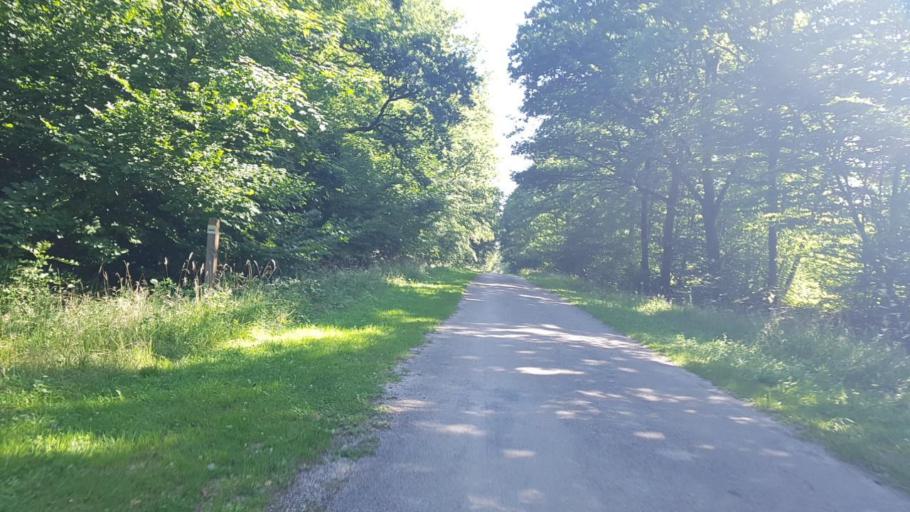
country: FR
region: Picardie
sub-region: Departement de l'Aisne
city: Hirson
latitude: 49.9394
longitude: 4.0941
